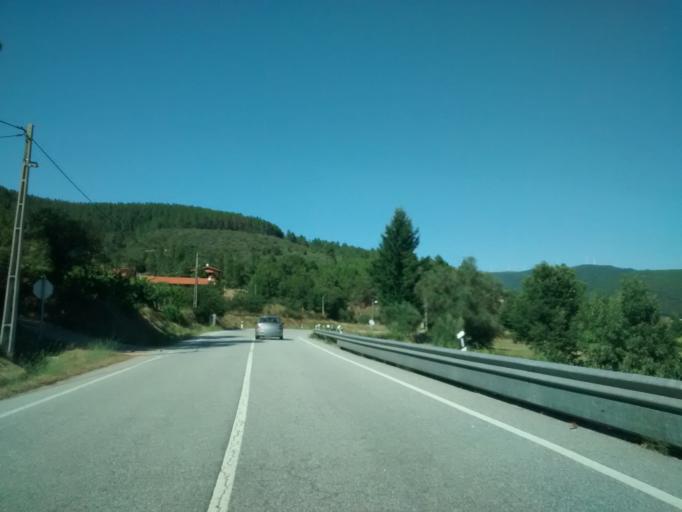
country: PT
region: Castelo Branco
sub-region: Belmonte
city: Belmonte
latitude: 40.3968
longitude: -7.4216
